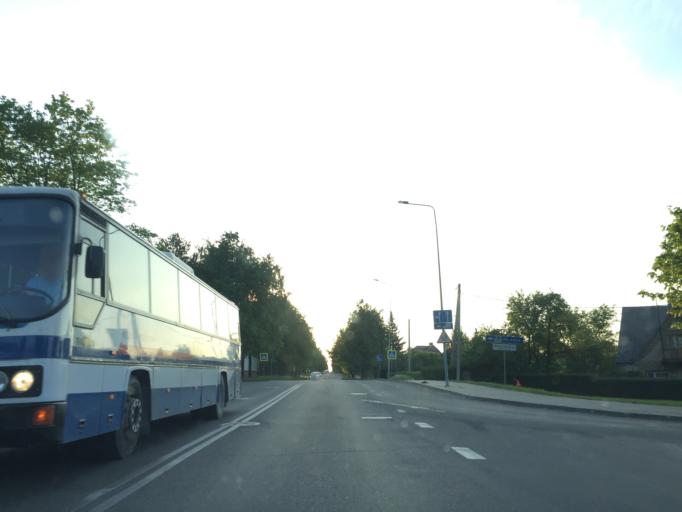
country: LT
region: Siauliu apskritis
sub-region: Siauliai
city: Siauliai
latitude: 55.9427
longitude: 23.3100
